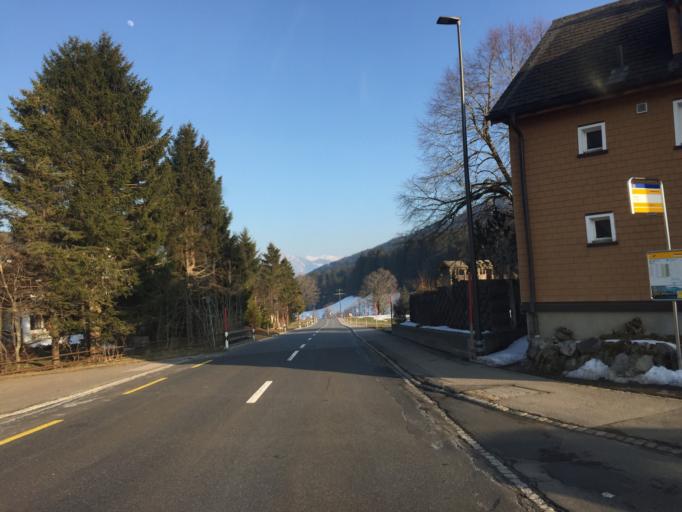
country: CH
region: Saint Gallen
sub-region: Wahlkreis Toggenburg
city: Wildhaus
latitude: 47.2004
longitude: 9.3609
